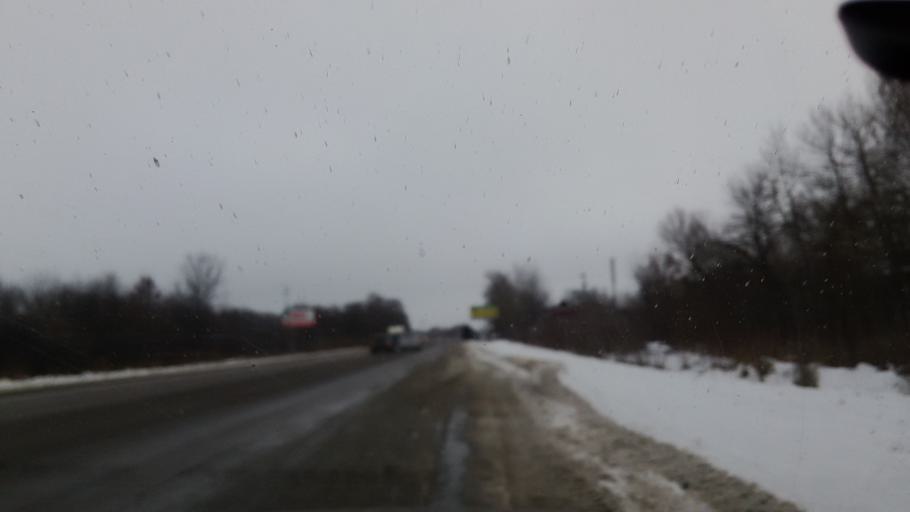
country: RU
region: Tula
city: Bolokhovo
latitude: 54.0654
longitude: 37.7990
